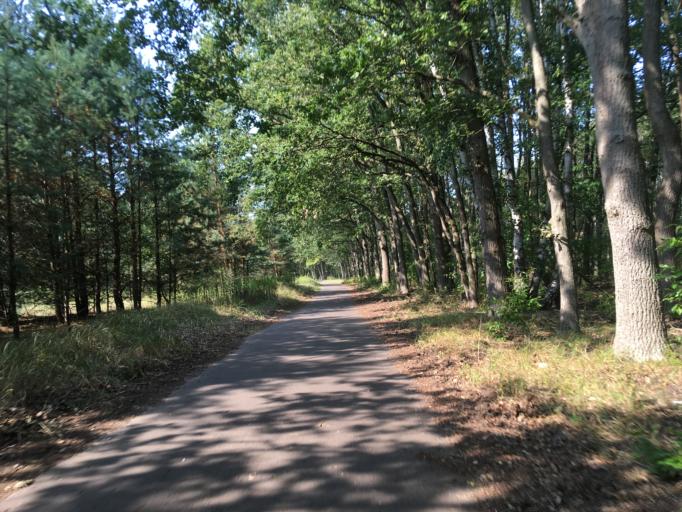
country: DE
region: Berlin
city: Falkenhagener Feld
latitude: 52.5943
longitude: 13.1805
